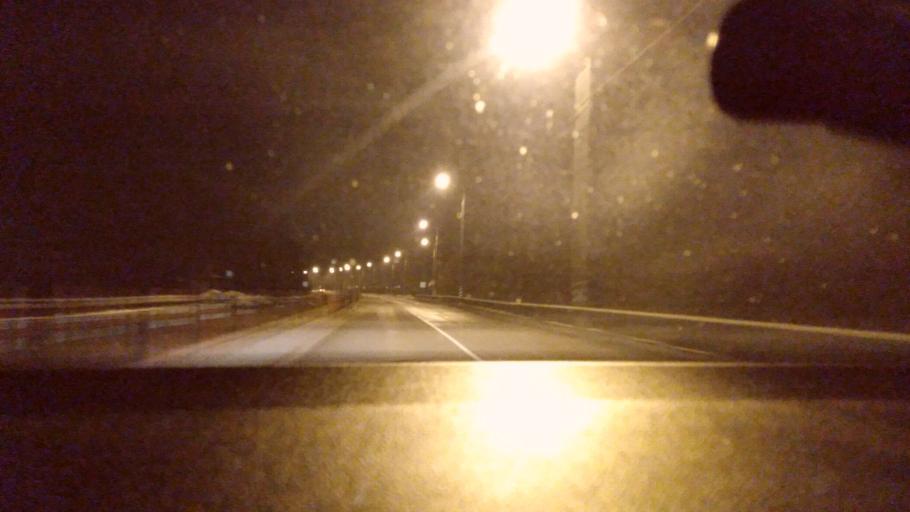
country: RU
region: Moskovskaya
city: Il'inskiy Pogost
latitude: 55.4855
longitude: 38.9214
